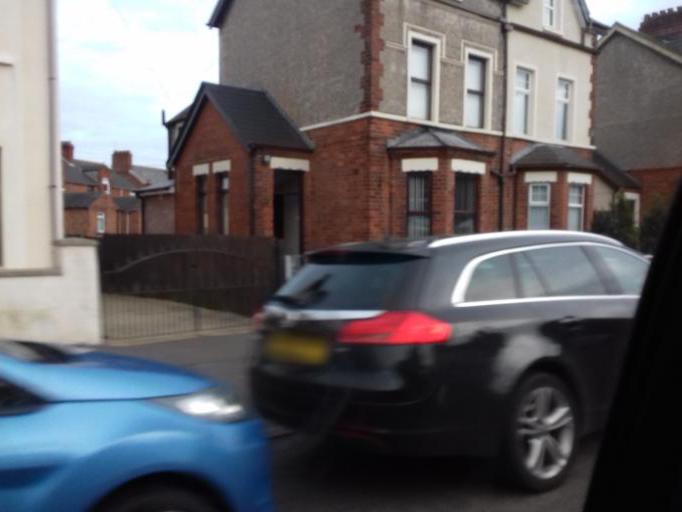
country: GB
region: Northern Ireland
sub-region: City of Belfast
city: Belfast
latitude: 54.6204
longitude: -5.9539
